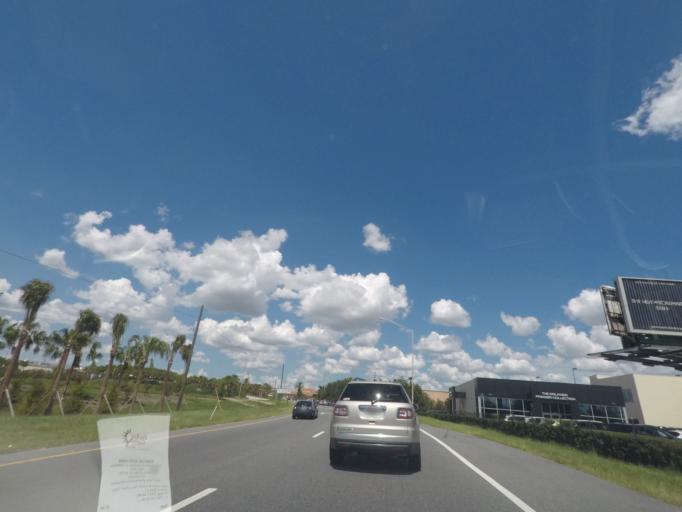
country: US
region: Florida
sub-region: Orange County
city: Oak Ridge
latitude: 28.4904
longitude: -81.4329
